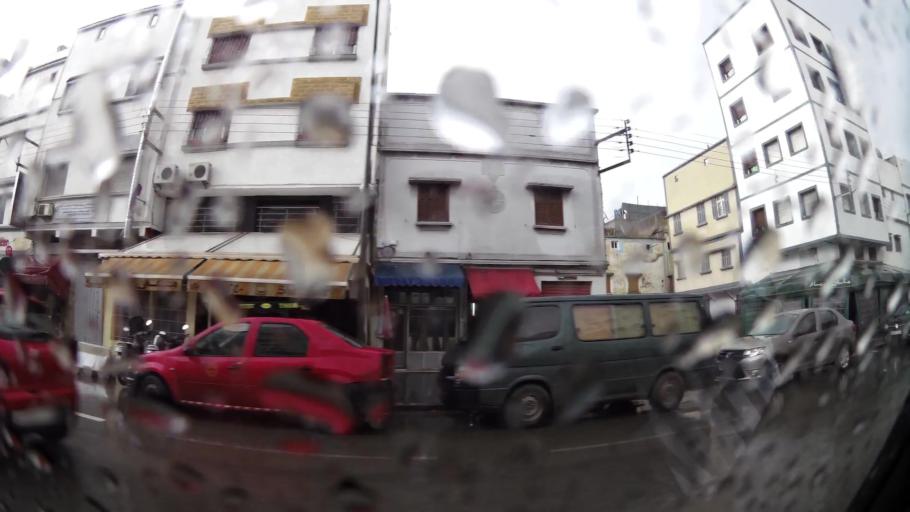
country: MA
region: Grand Casablanca
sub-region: Casablanca
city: Casablanca
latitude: 33.5487
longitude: -7.5787
